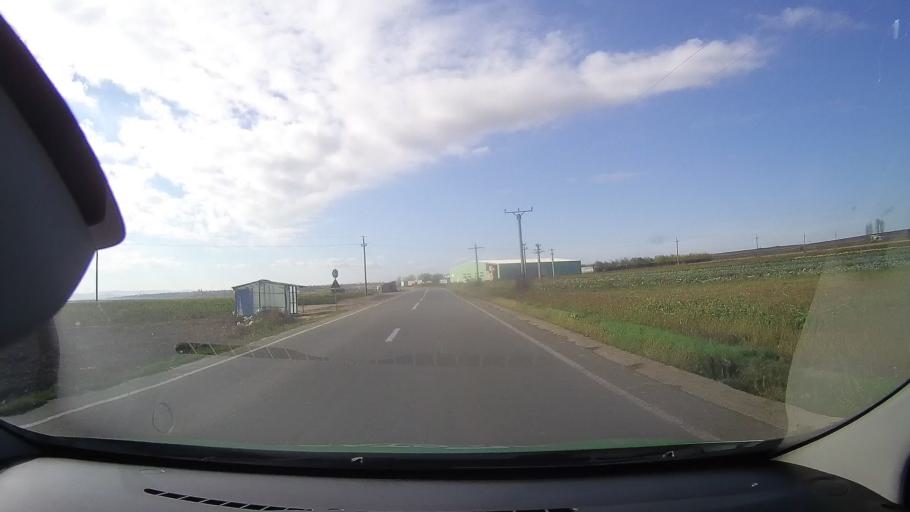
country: RO
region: Tulcea
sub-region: Comuna Sarichioi
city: Sarichioi
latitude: 44.9695
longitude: 28.8704
